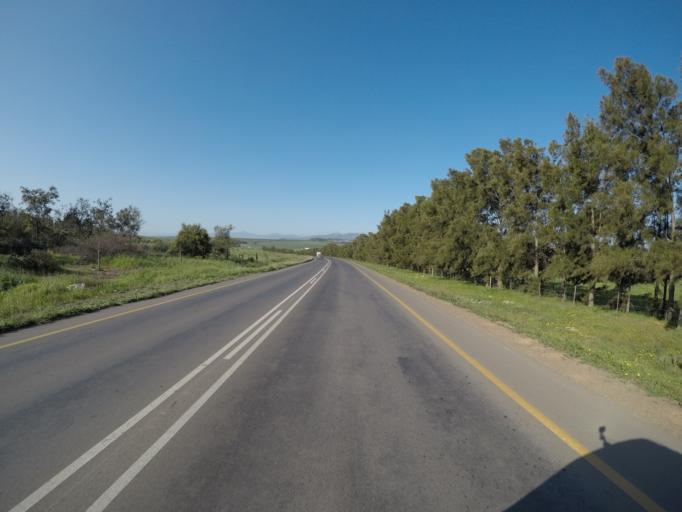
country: ZA
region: Western Cape
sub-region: City of Cape Town
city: Kraaifontein
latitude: -33.7742
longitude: 18.7491
